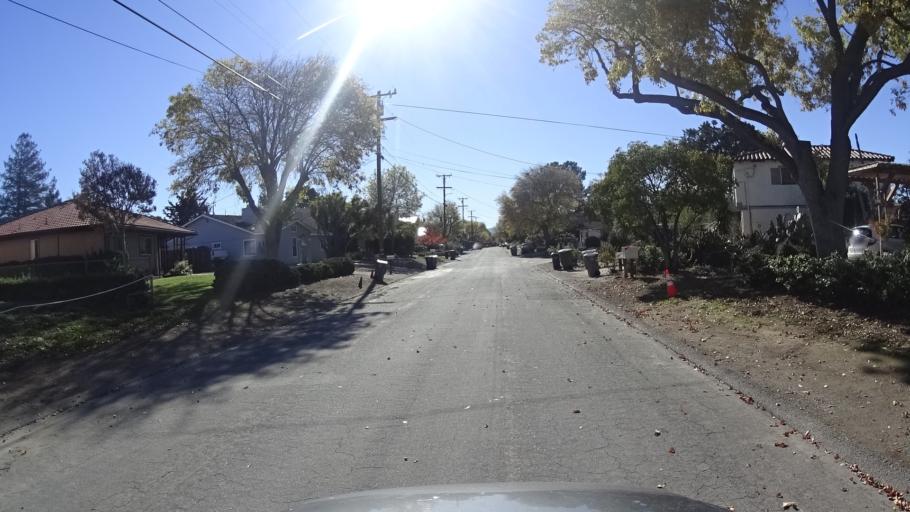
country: US
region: California
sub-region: Santa Clara County
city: Sunnyvale
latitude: 37.3503
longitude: -122.0111
